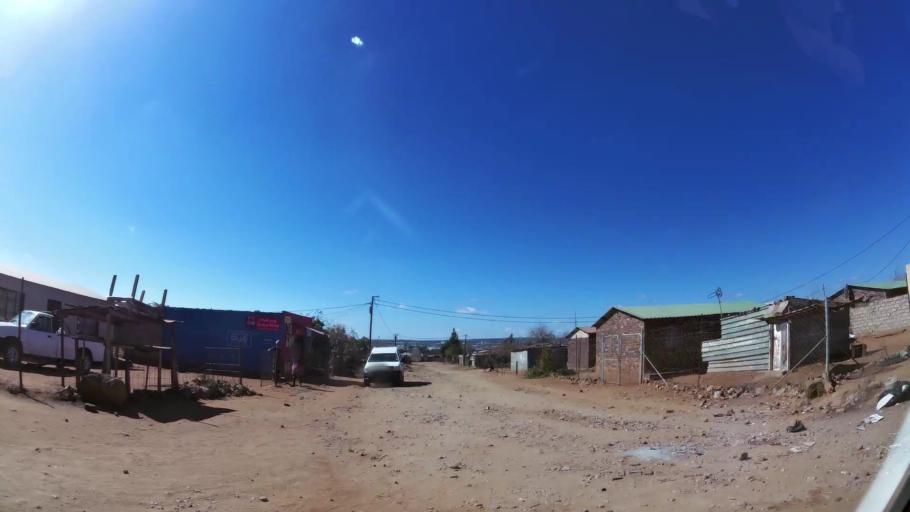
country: ZA
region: Limpopo
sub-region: Capricorn District Municipality
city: Polokwane
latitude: -23.8914
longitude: 29.4133
